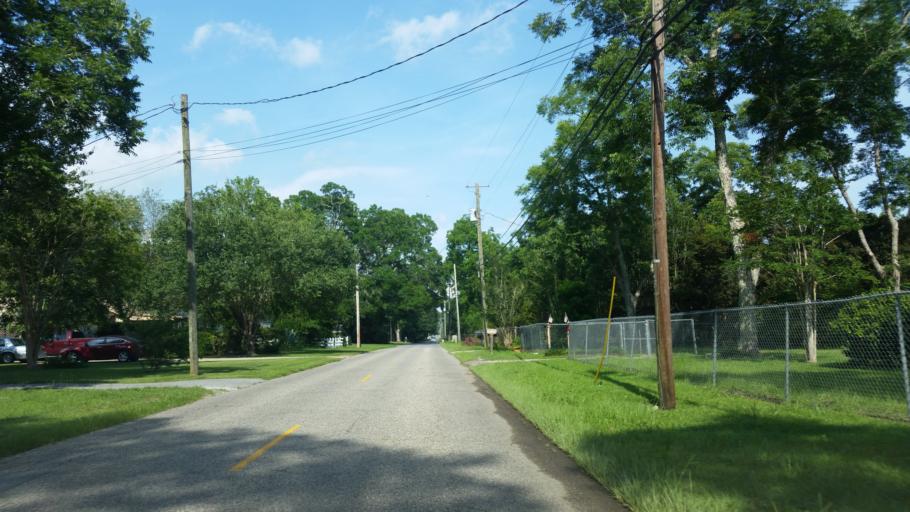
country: US
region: Florida
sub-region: Escambia County
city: Ensley
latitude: 30.5411
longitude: -87.2977
